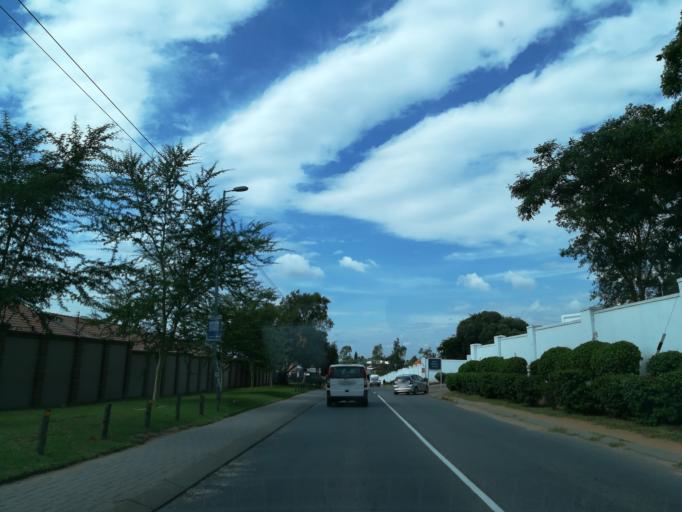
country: ZA
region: Gauteng
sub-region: West Rand District Municipality
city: Muldersdriseloop
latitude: -26.0566
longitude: 27.9617
